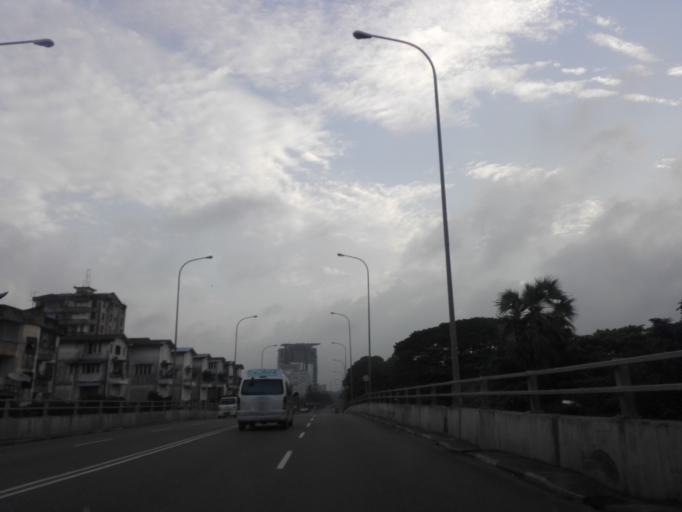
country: MM
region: Yangon
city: Yangon
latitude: 16.8273
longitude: 96.1310
